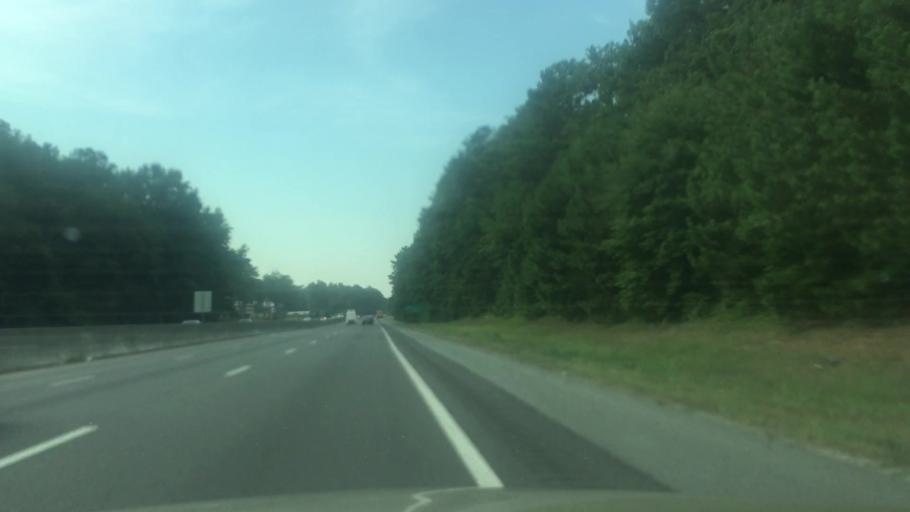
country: US
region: South Carolina
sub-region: Lexington County
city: Springdale
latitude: 33.9644
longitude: -81.0976
